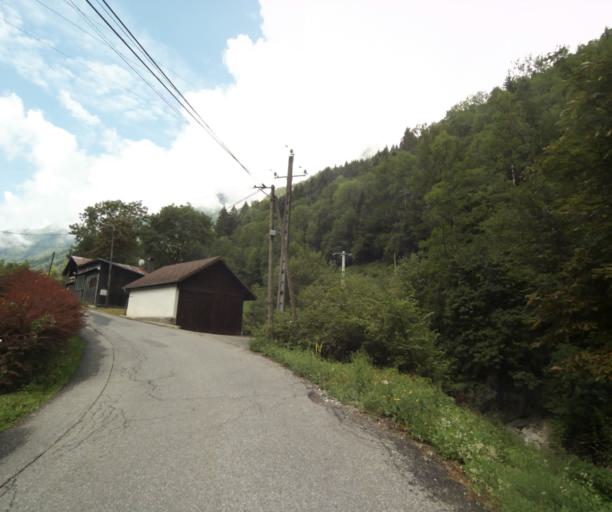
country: FR
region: Rhone-Alpes
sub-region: Departement de la Haute-Savoie
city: Thones
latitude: 45.8764
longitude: 6.2944
